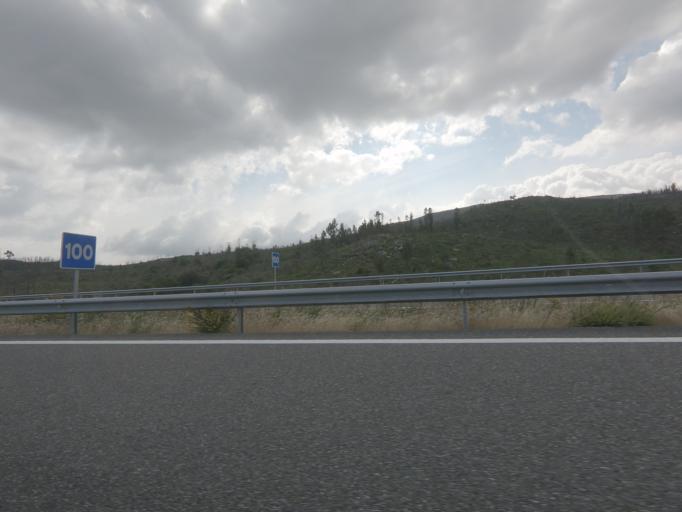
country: ES
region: Galicia
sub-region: Provincia de Ourense
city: Melon
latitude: 42.2768
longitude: -8.2031
